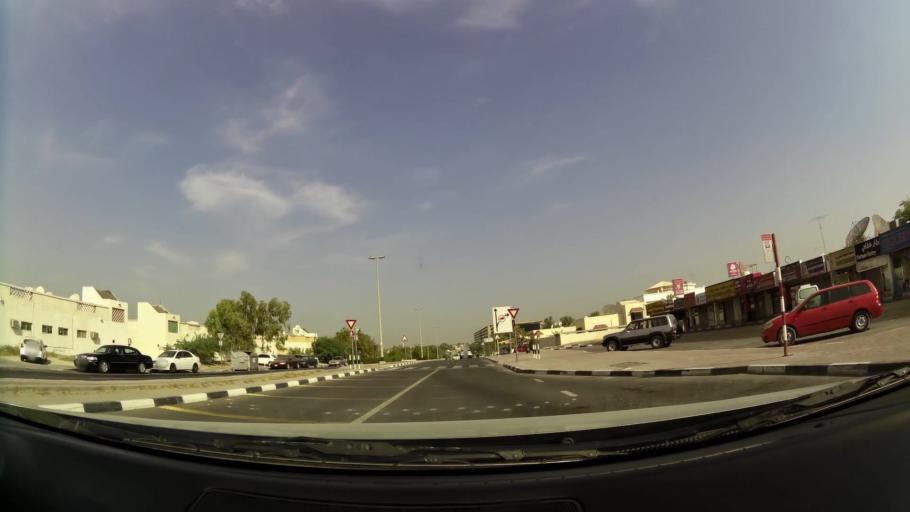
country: AE
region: Ash Shariqah
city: Sharjah
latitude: 25.2270
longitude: 55.3968
